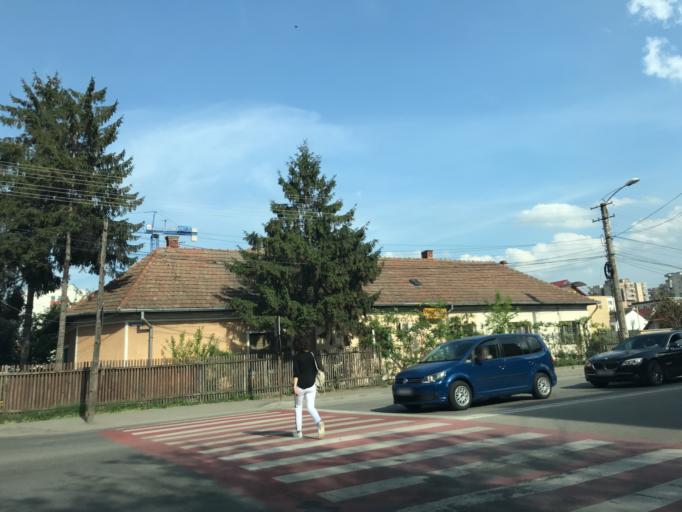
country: RO
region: Cluj
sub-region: Municipiul Cluj-Napoca
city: Cluj-Napoca
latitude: 46.7821
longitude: 23.6192
